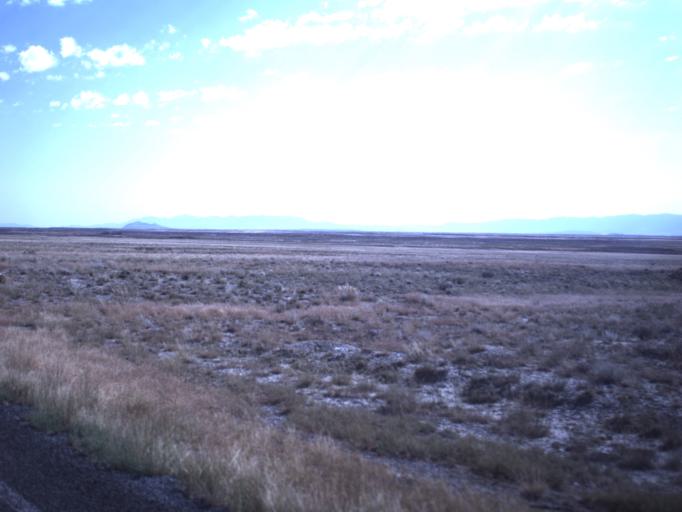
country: US
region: Utah
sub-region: Beaver County
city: Milford
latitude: 38.8656
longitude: -112.8371
